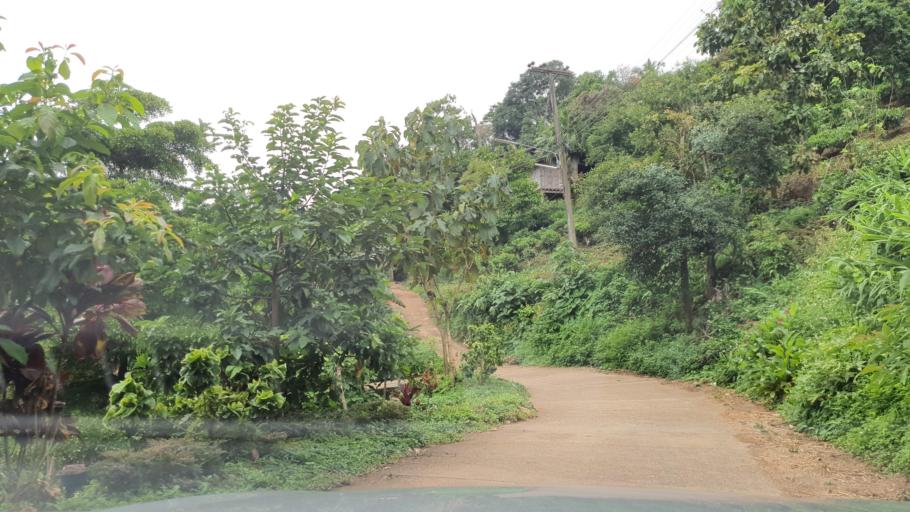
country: TH
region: Chiang Mai
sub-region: Amphoe Chiang Dao
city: Chiang Dao
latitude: 19.2589
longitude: 98.9211
